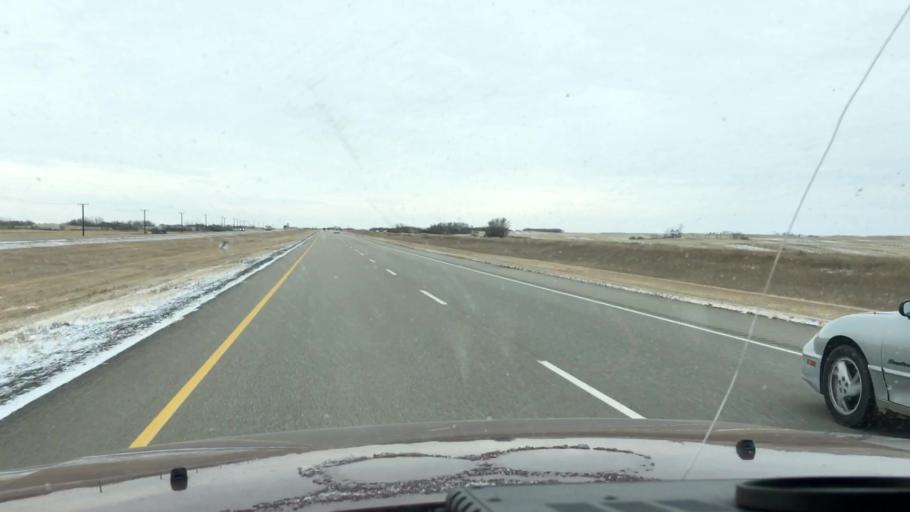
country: CA
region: Saskatchewan
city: Watrous
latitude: 51.4001
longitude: -106.1763
